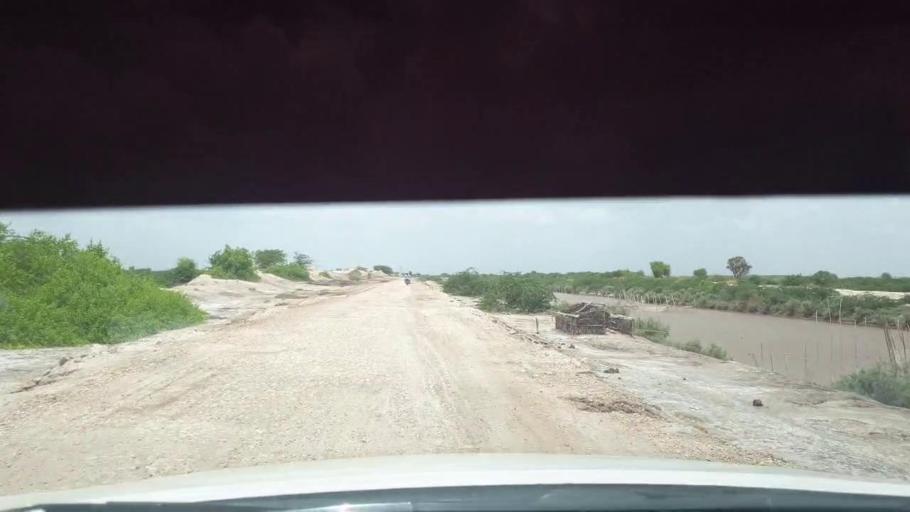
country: PK
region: Sindh
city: Kadhan
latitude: 24.5159
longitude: 69.1205
